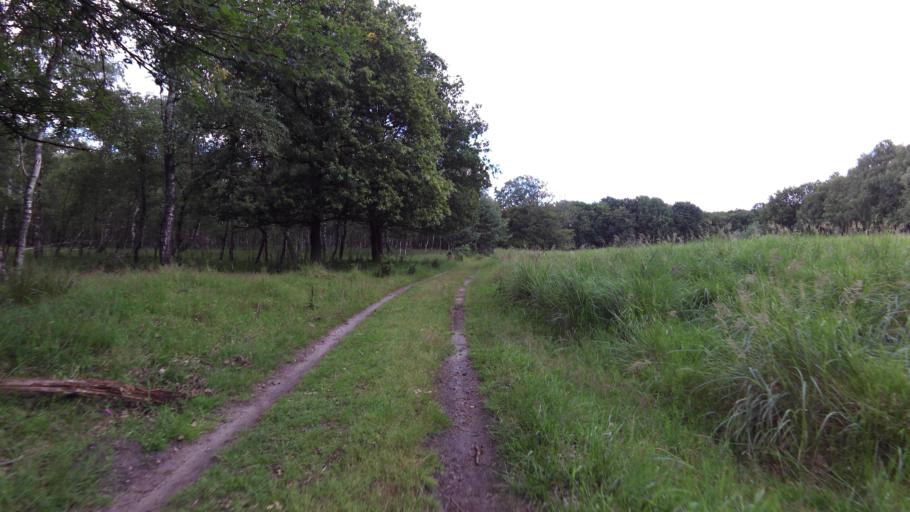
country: NL
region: Gelderland
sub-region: Gemeente Apeldoorn
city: Uddel
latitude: 52.2284
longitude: 5.8306
